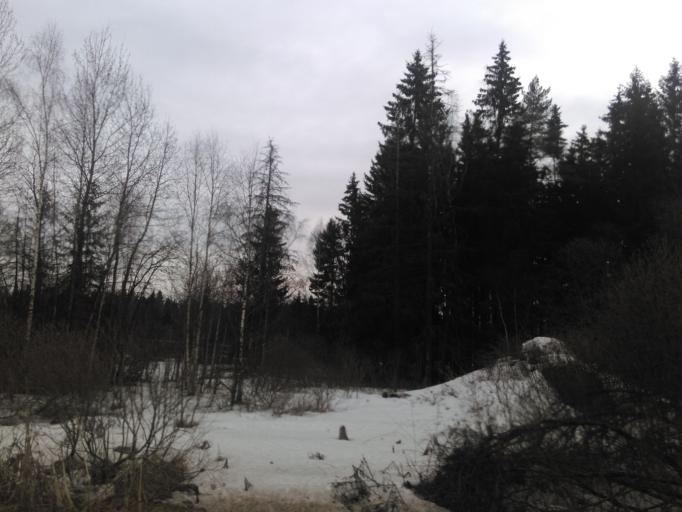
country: RU
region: Moskovskaya
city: Kolyubakino
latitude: 55.6896
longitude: 36.5667
